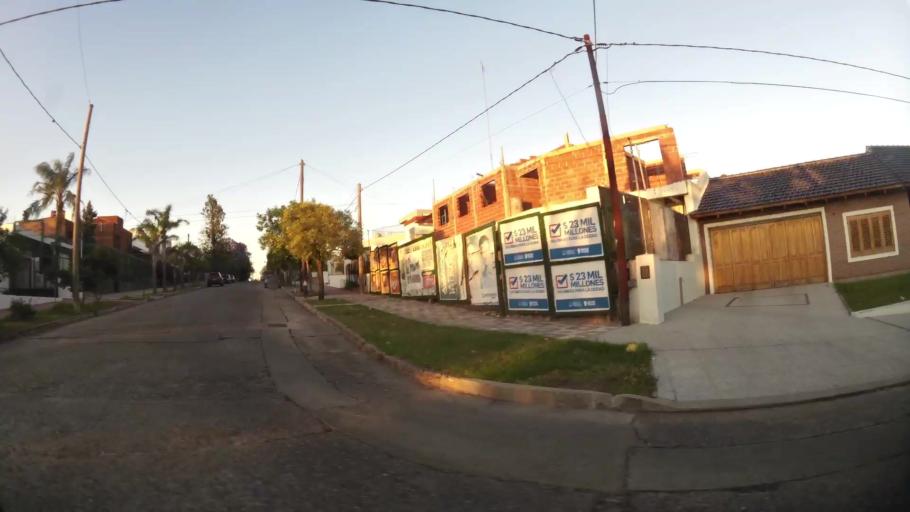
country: AR
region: Cordoba
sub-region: Departamento de Capital
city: Cordoba
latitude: -31.3814
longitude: -64.2181
